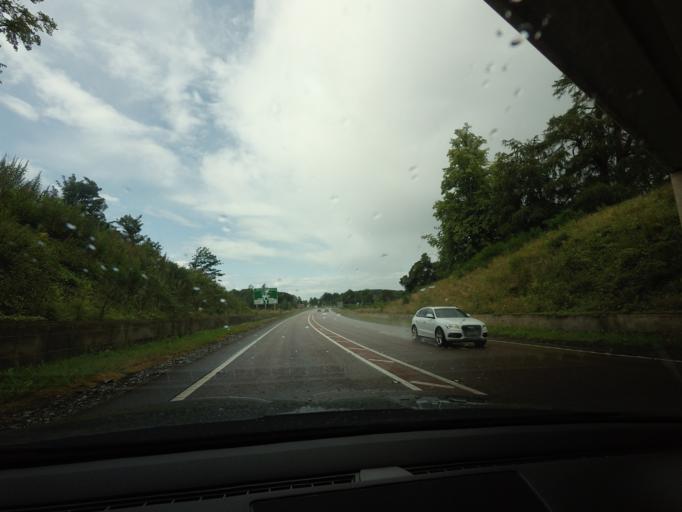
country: GB
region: Scotland
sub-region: Moray
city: Fochabers
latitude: 57.6173
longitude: -3.1010
